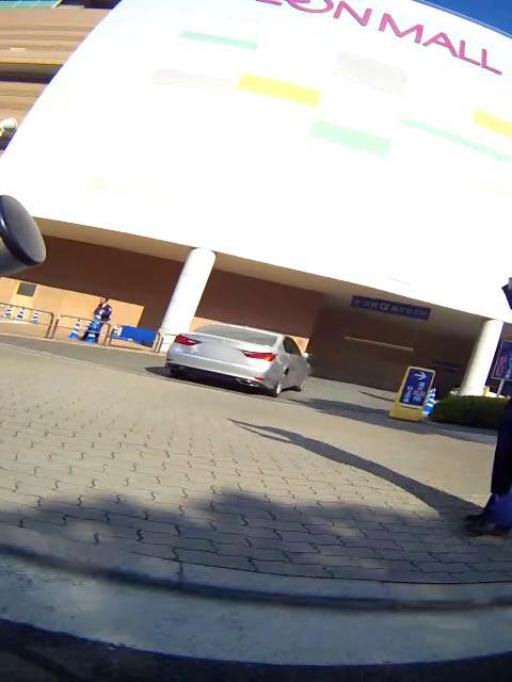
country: JP
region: Osaka
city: Moriguchi
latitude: 34.7030
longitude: 135.5663
